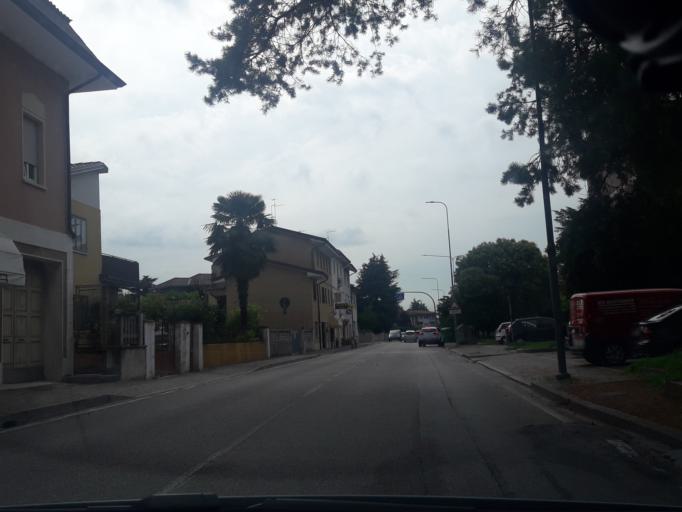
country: IT
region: Friuli Venezia Giulia
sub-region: Provincia di Udine
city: Colugna
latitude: 46.0717
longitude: 13.2132
